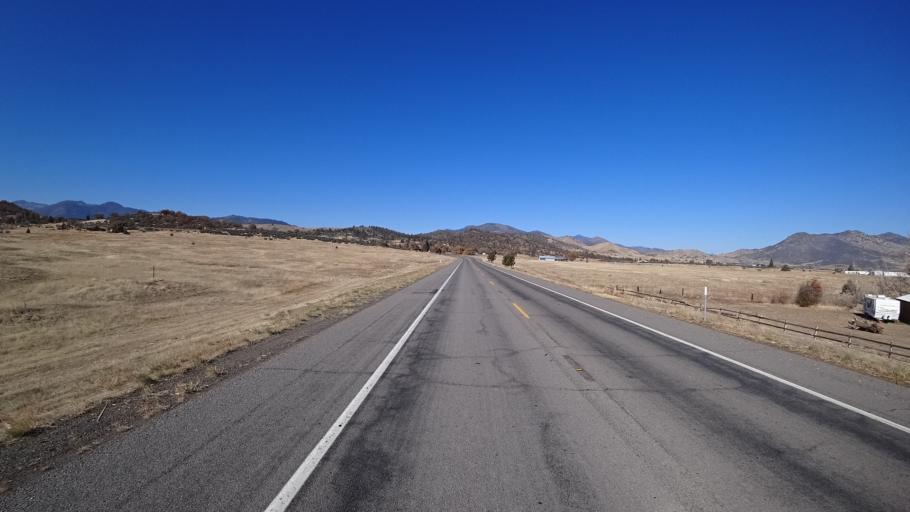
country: US
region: California
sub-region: Siskiyou County
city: Yreka
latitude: 41.7381
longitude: -122.5962
